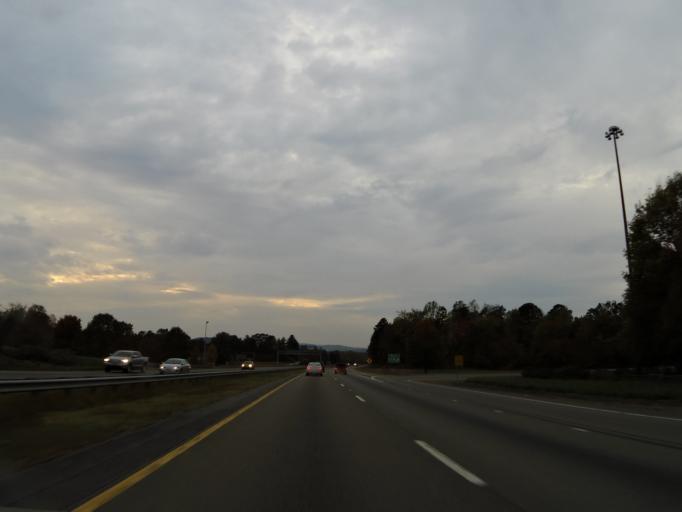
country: US
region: North Carolina
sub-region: Burke County
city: Hildebran
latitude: 35.7054
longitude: -81.4239
